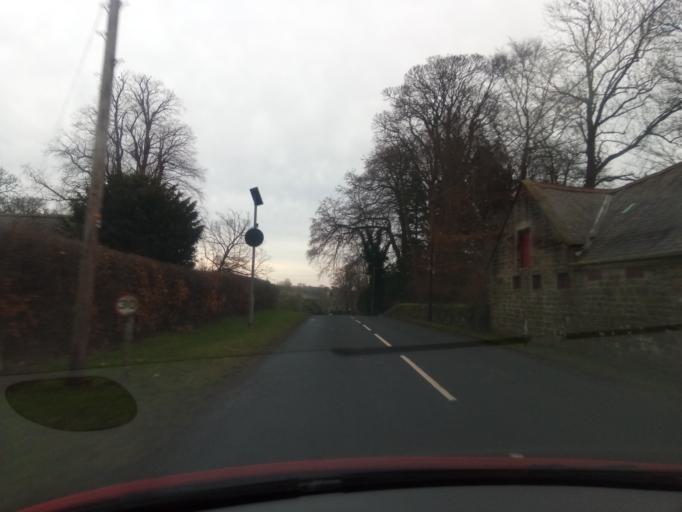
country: GB
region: England
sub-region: Northumberland
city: Whittingham
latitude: 55.4704
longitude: -1.8368
